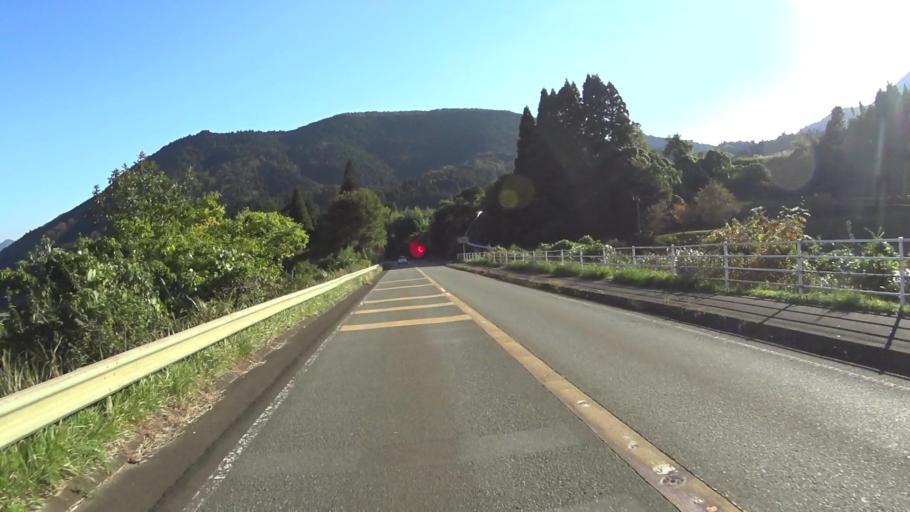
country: JP
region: Kyoto
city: Fukuchiyama
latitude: 35.4025
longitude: 135.0821
